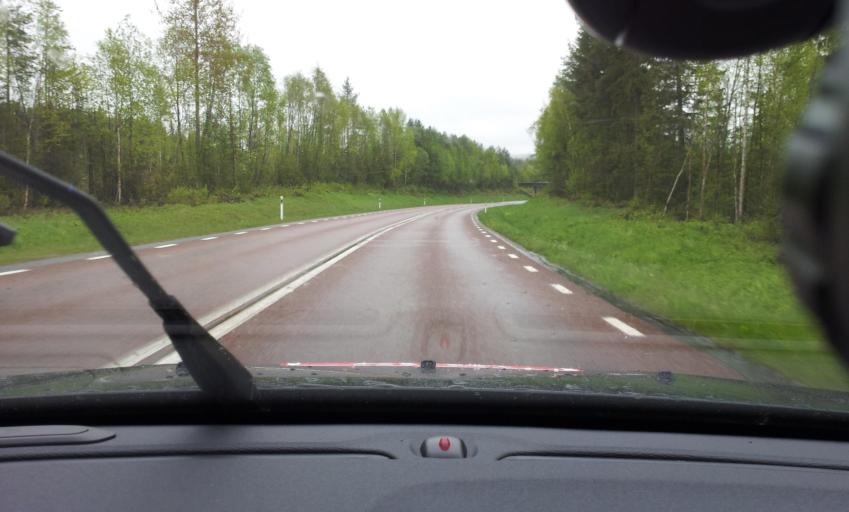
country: SE
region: Jaemtland
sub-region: Bergs Kommun
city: Hoverberg
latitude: 62.7576
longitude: 14.4371
